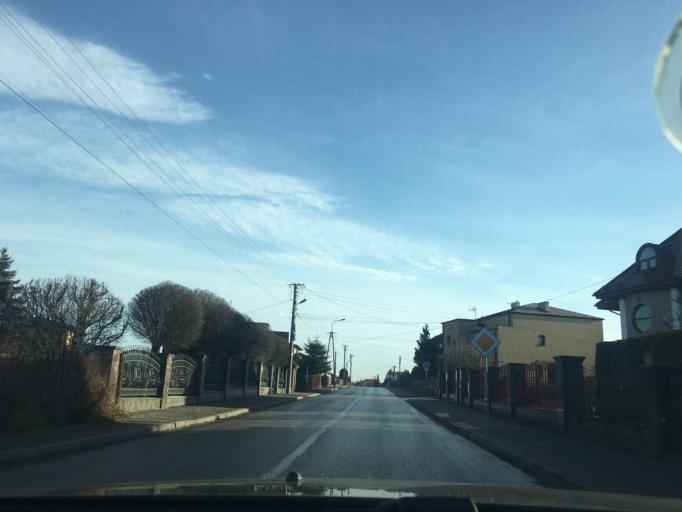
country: PL
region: Swietokrzyskie
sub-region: Powiat jedrzejowski
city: Jedrzejow
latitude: 50.6365
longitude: 20.3072
